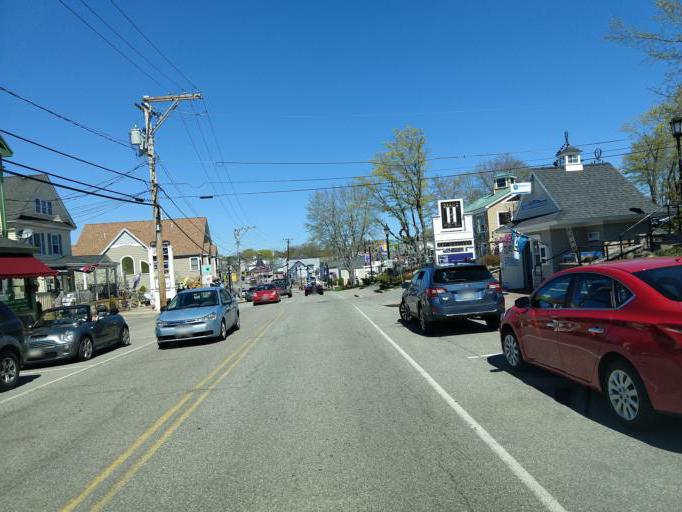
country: US
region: Maine
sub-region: York County
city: Kennebunkport
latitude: 43.3599
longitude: -70.4807
